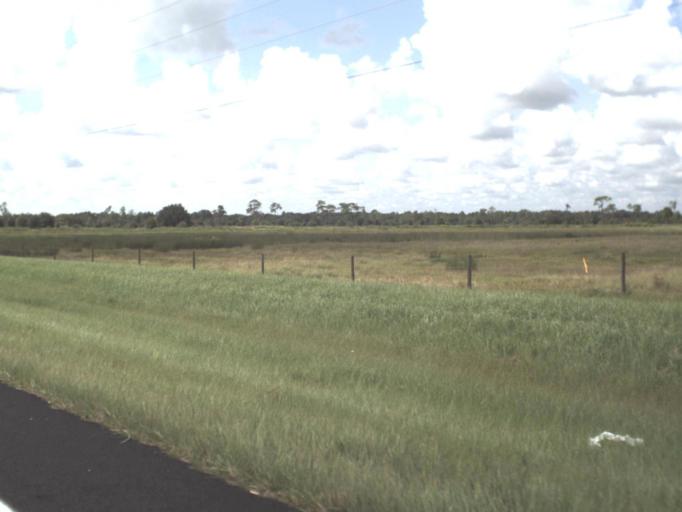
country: US
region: Florida
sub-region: Hardee County
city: Zolfo Springs
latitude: 27.4331
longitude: -81.7963
